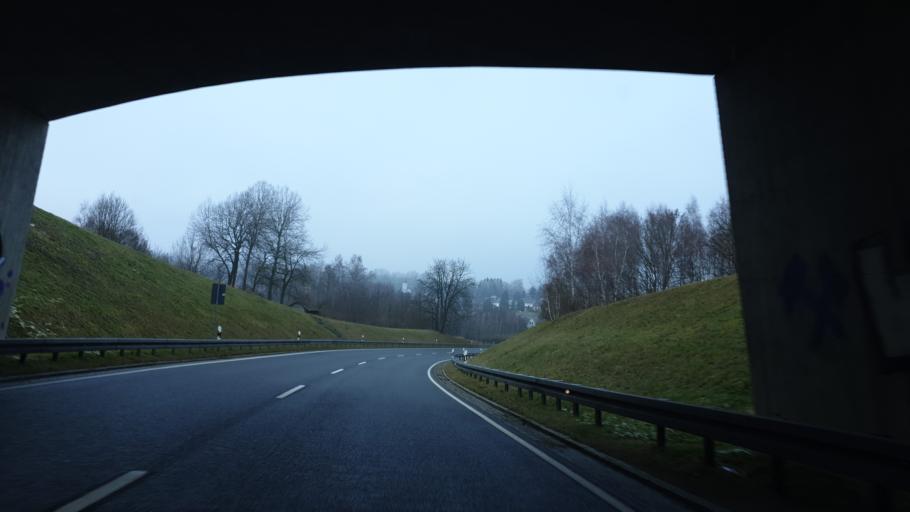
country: DE
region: Saxony
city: Bad Brambach
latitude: 50.2179
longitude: 12.3188
